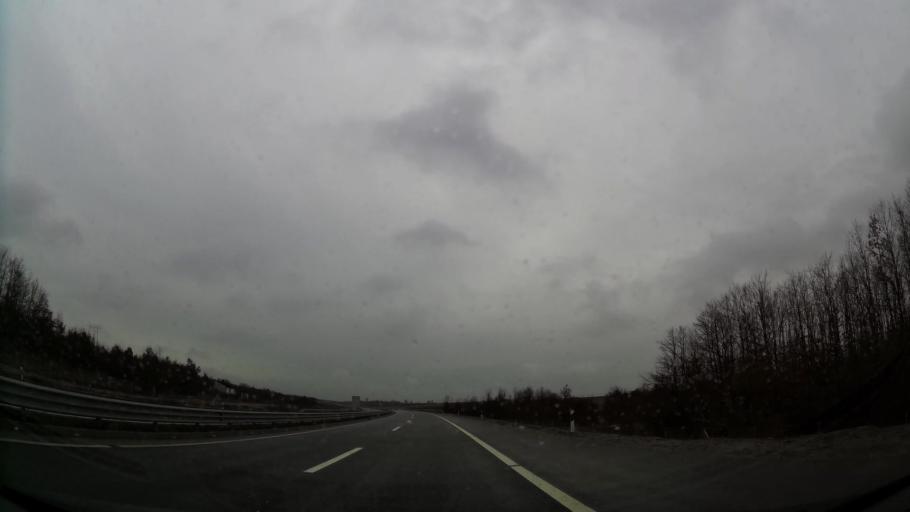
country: XK
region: Ferizaj
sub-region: Komuna e Ferizajt
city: Ferizaj
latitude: 42.3602
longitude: 21.2020
